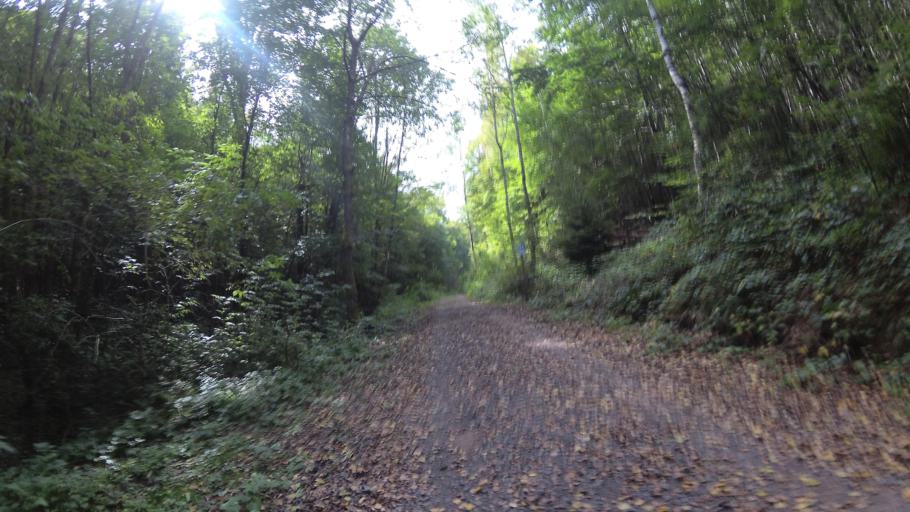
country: DE
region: Saarland
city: Friedrichsthal
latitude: 49.3027
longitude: 7.1043
